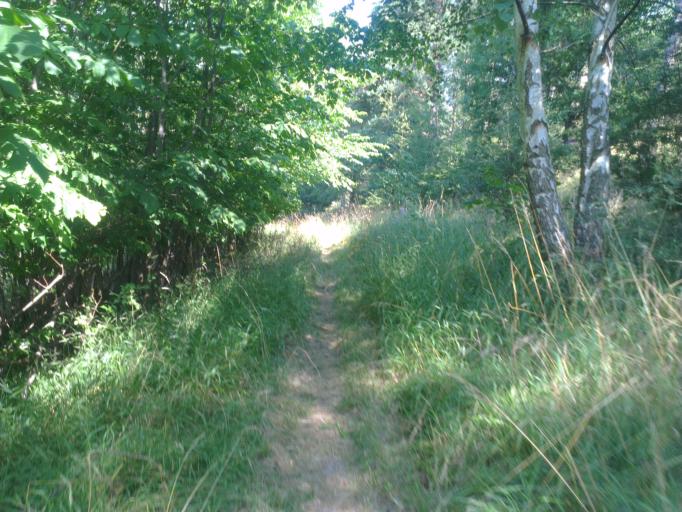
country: DK
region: Capital Region
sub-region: Frederikssund Kommune
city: Skibby
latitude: 55.7754
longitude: 12.0306
